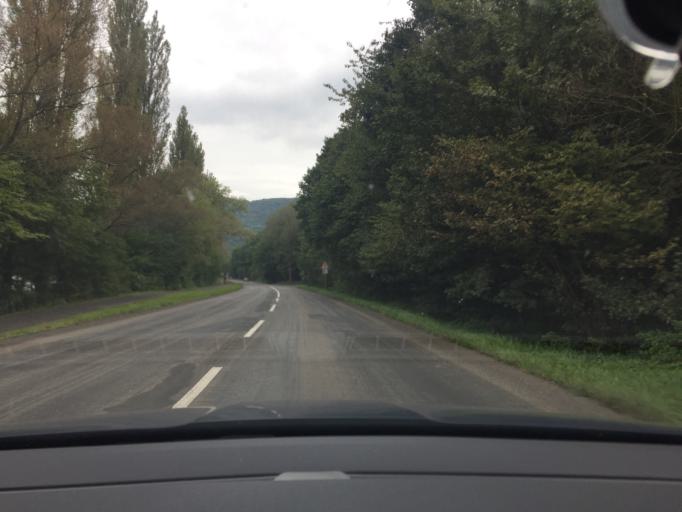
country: CZ
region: Ustecky
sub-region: Okres Usti nad Labem
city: Usti nad Labem
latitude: 50.6084
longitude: 14.0762
